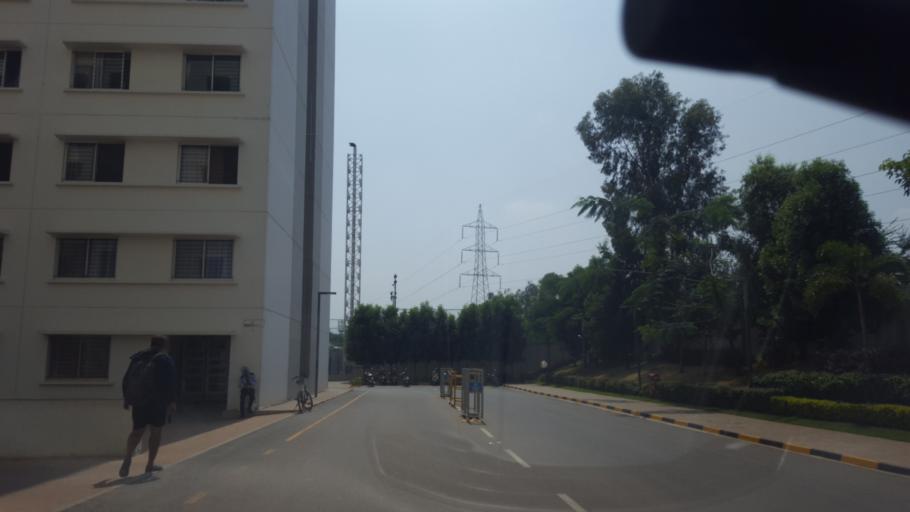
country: IN
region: Karnataka
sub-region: Bangalore Urban
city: Bangalore
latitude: 12.9384
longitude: 77.7202
